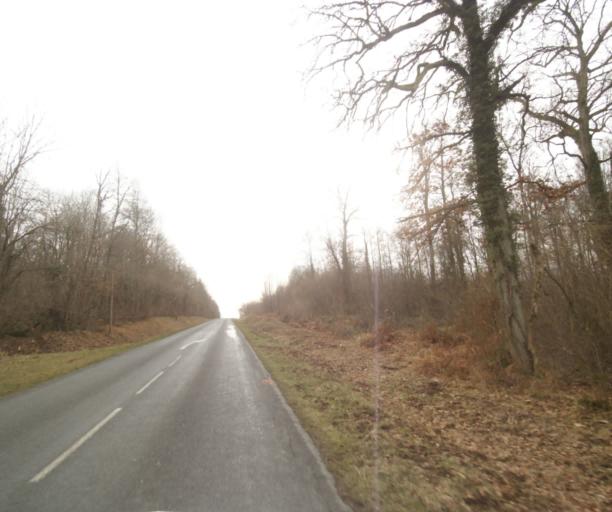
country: FR
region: Champagne-Ardenne
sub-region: Departement de la Haute-Marne
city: Villiers-en-Lieu
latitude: 48.7028
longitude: 4.8939
